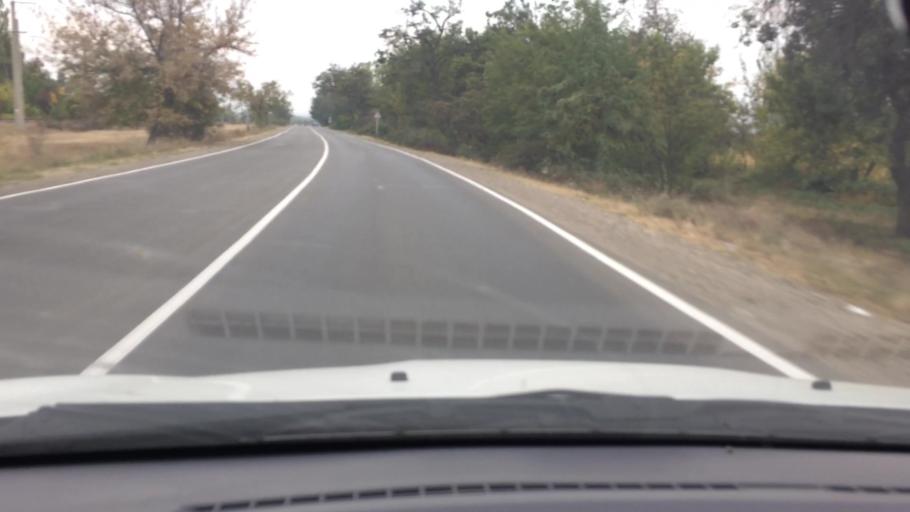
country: GE
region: Kvemo Kartli
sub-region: Marneuli
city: Marneuli
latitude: 41.4157
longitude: 44.8269
